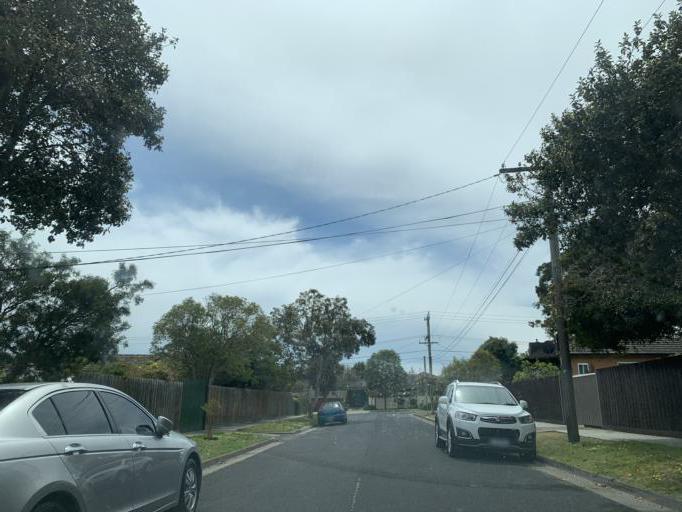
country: AU
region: Victoria
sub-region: Bayside
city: Highett
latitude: -37.9513
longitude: 145.0258
